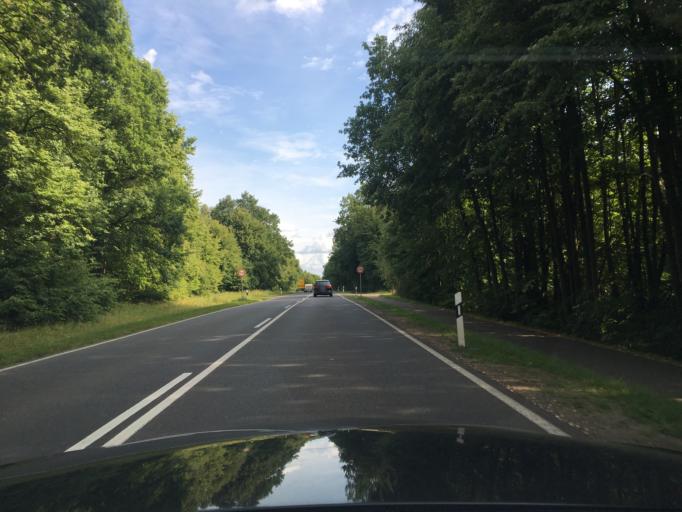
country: DE
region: Mecklenburg-Vorpommern
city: Neustrelitz
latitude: 53.3890
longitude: 13.0464
